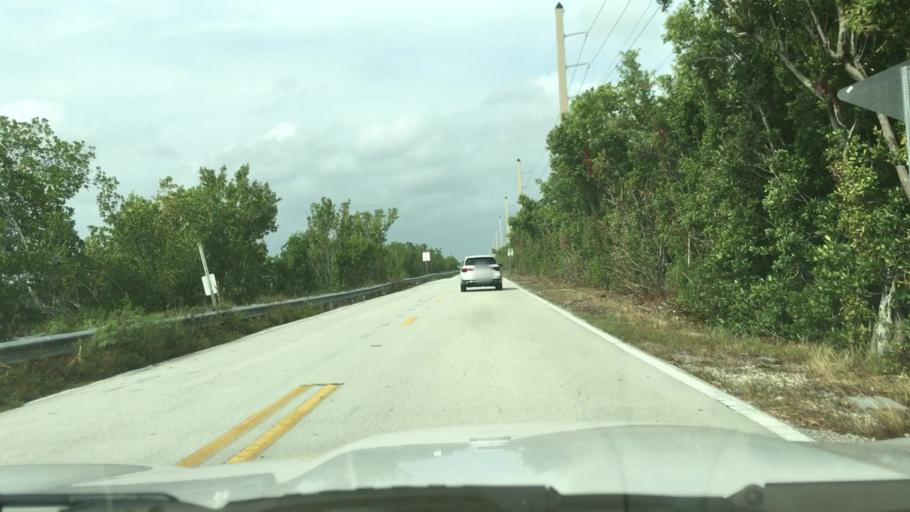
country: US
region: Florida
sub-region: Monroe County
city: North Key Largo
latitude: 25.3017
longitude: -80.3874
